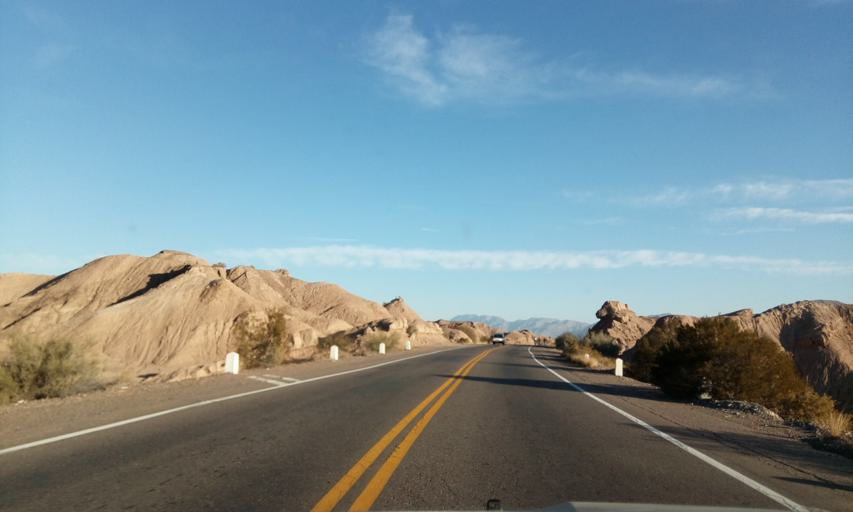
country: AR
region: San Juan
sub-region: Departamento de Rivadavia
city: Rivadavia
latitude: -31.4538
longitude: -68.6373
